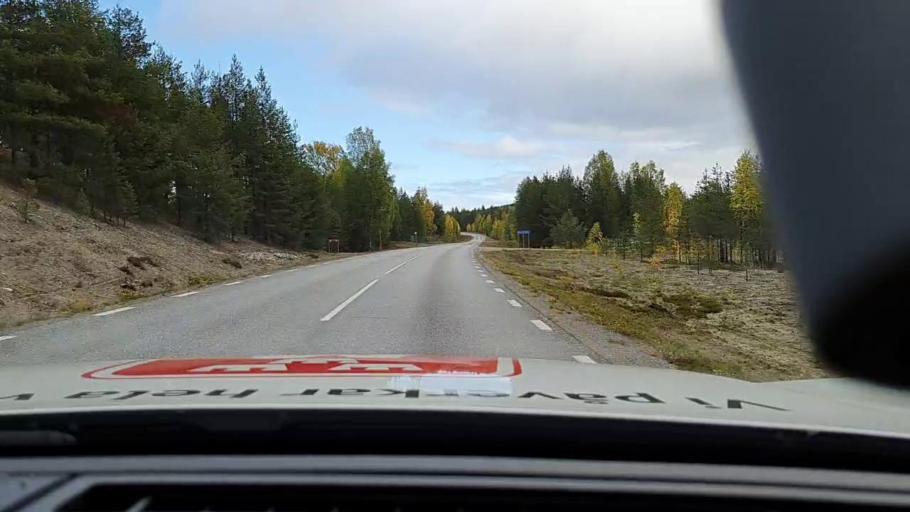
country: SE
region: Vaesterbotten
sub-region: Norsjo Kommun
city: Norsjoe
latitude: 64.9656
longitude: 19.7025
